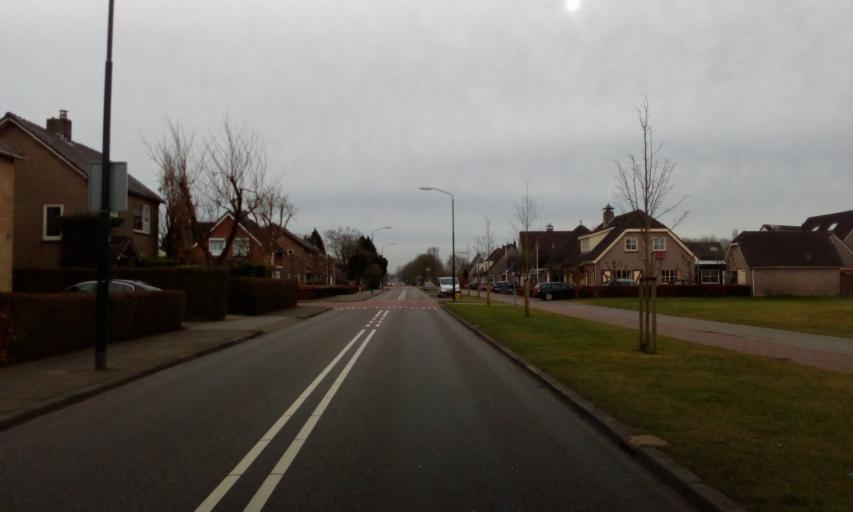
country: NL
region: North Brabant
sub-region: Gemeente Woudrichem
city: Woudrichem
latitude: 51.7910
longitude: 5.0287
